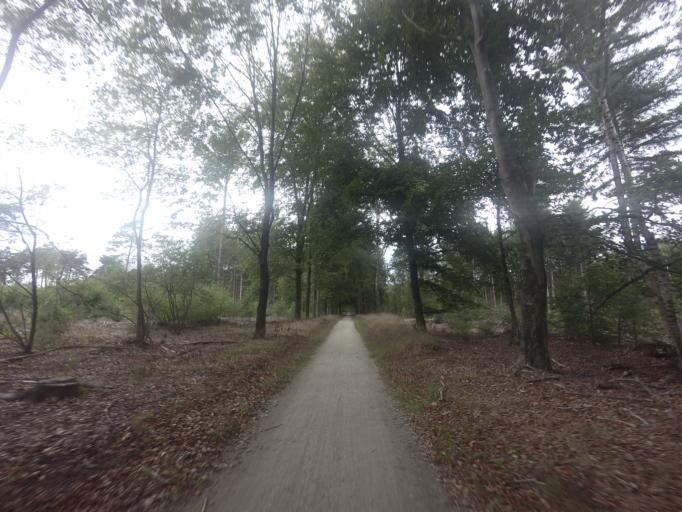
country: NL
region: Drenthe
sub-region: Gemeente Westerveld
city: Dwingeloo
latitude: 52.9250
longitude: 6.3384
